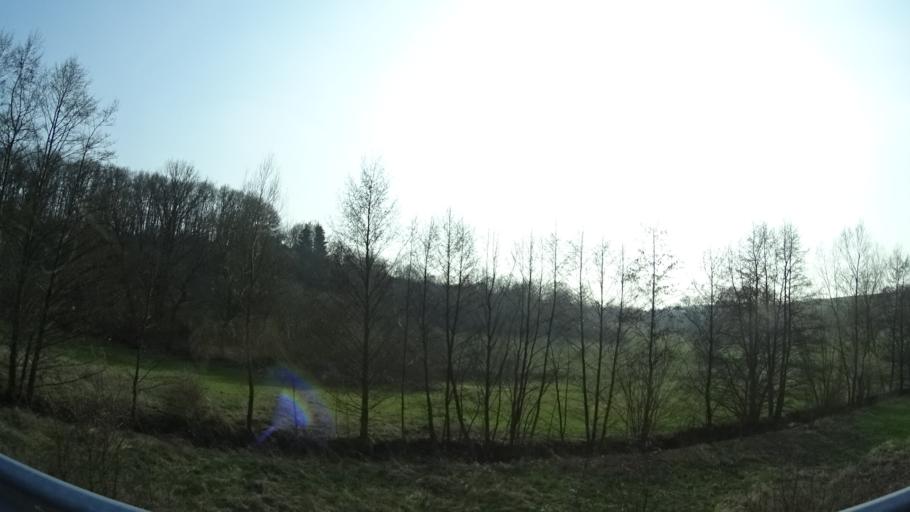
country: DE
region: Rheinland-Pfalz
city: Oberstaufenbach
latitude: 49.5078
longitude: 7.5195
